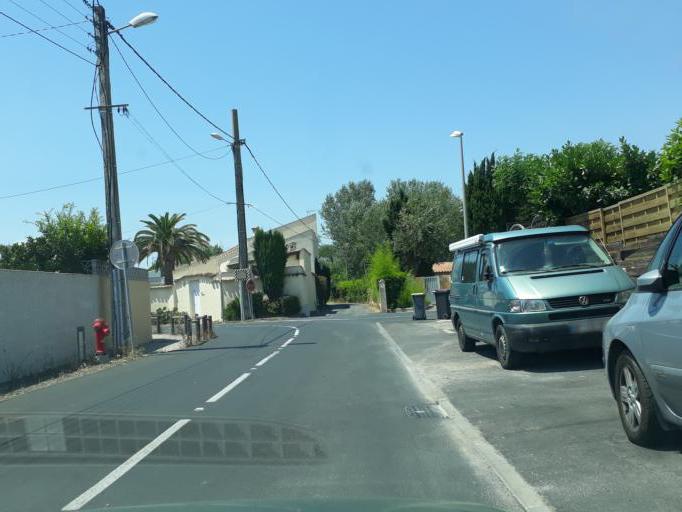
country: FR
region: Languedoc-Roussillon
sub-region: Departement de l'Herault
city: Agde
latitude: 43.2915
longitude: 3.4523
